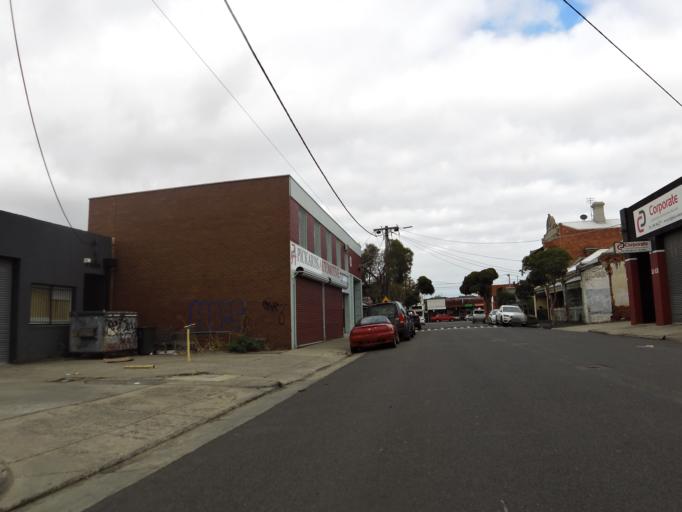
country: AU
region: Victoria
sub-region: Yarra
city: Richmond
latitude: -37.8099
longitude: 145.0034
